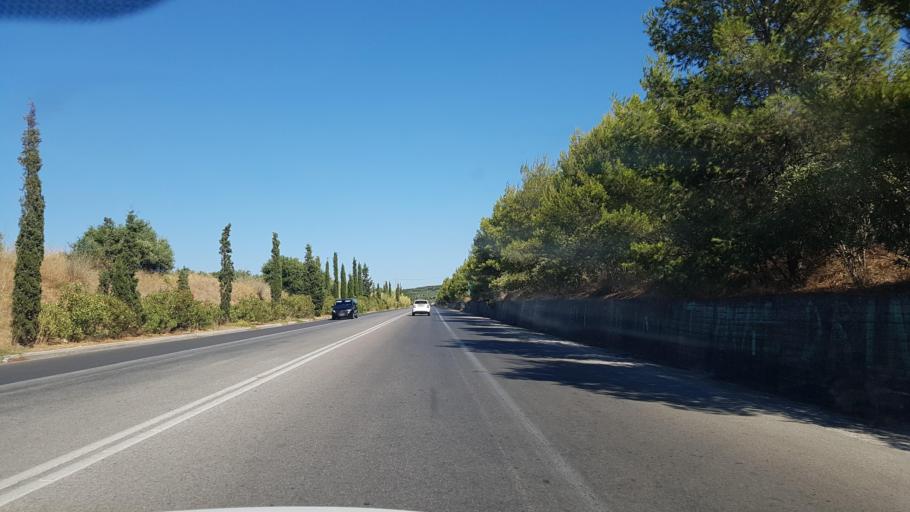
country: GR
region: Crete
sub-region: Nomos Chanias
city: Kolympari
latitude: 35.5284
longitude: 23.7934
